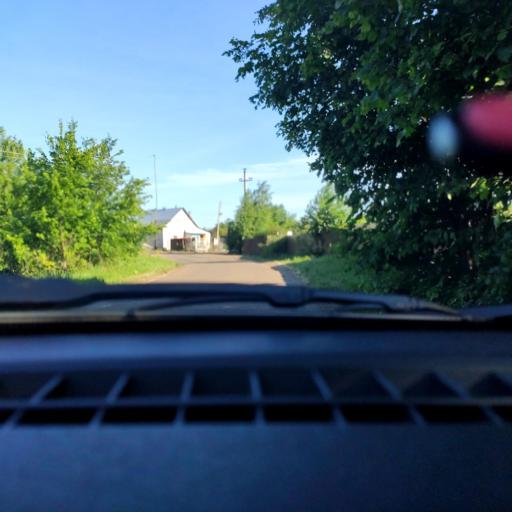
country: RU
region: Bashkortostan
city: Avdon
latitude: 54.4629
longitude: 55.8376
